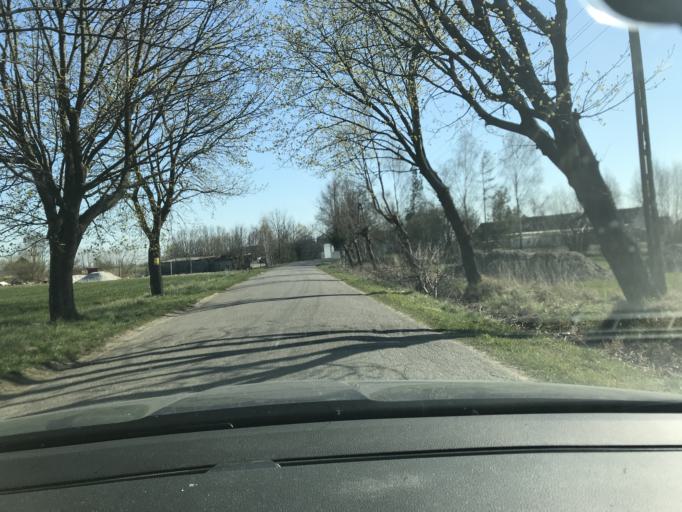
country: PL
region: Pomeranian Voivodeship
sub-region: Powiat nowodworski
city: Sztutowo
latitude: 54.3127
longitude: 19.1601
